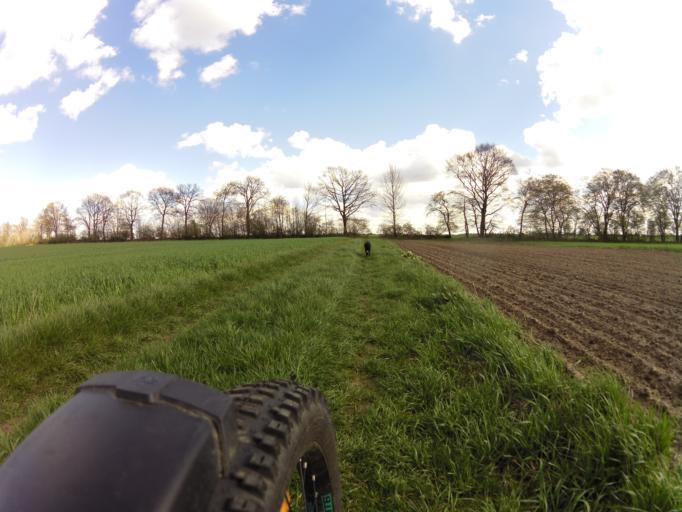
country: PL
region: West Pomeranian Voivodeship
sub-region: Powiat gryficki
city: Ploty
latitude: 53.8312
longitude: 15.2581
